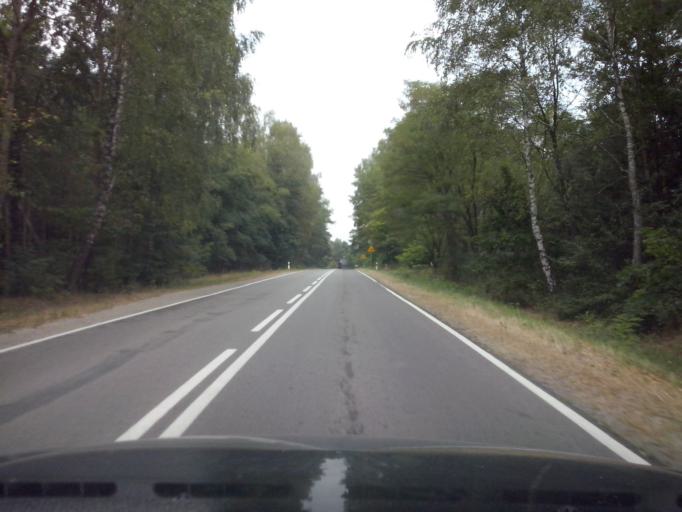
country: PL
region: Swietokrzyskie
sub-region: Powiat kielecki
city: Rakow
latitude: 50.6994
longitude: 21.0585
